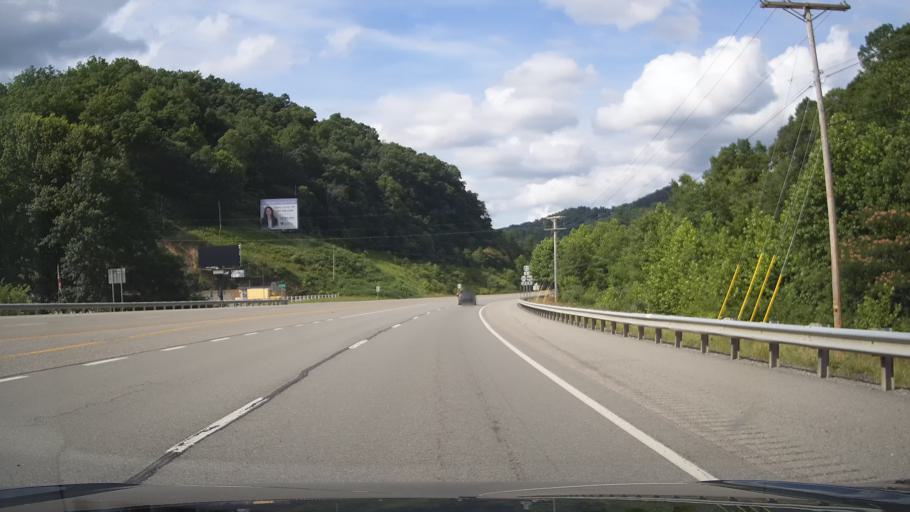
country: US
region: Kentucky
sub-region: Floyd County
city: Prestonsburg
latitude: 37.7178
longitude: -82.7912
